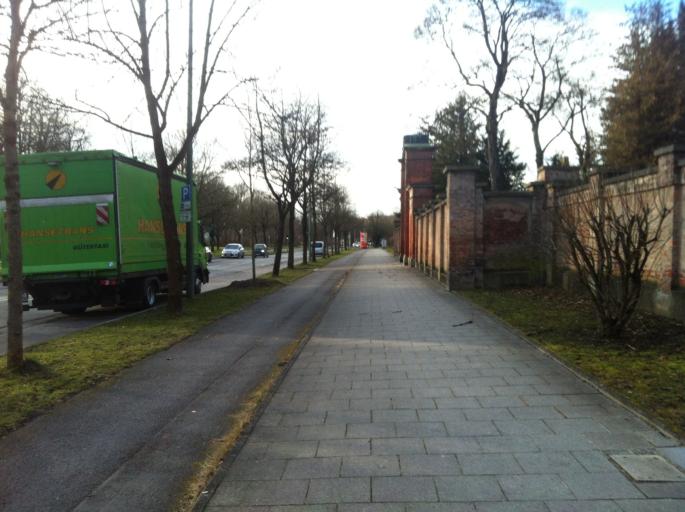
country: DE
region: Bavaria
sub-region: Upper Bavaria
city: Munich
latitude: 48.1098
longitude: 11.5468
